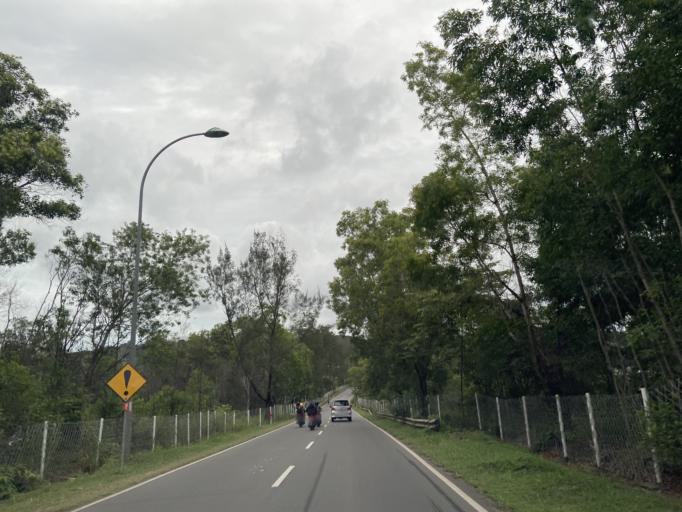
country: SG
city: Singapore
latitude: 1.1130
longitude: 104.0132
